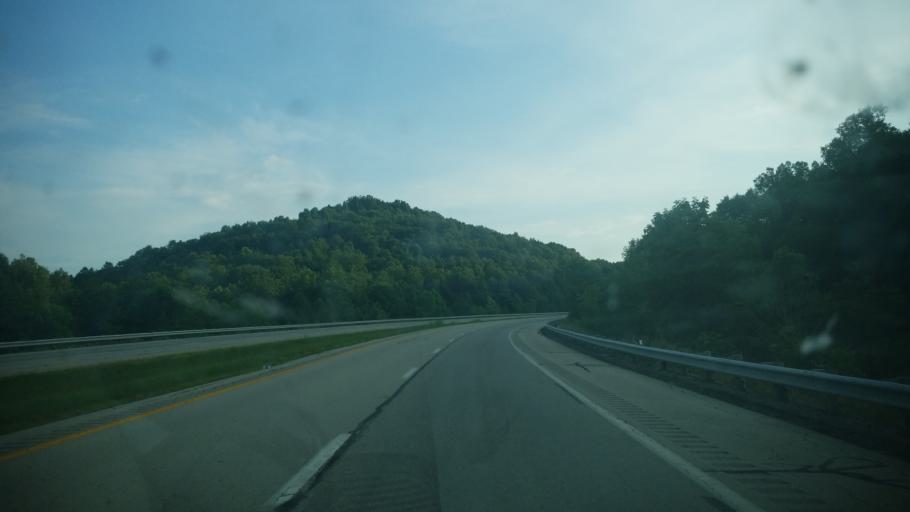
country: US
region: Ohio
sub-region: Adams County
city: Peebles
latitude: 39.0338
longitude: -83.2605
